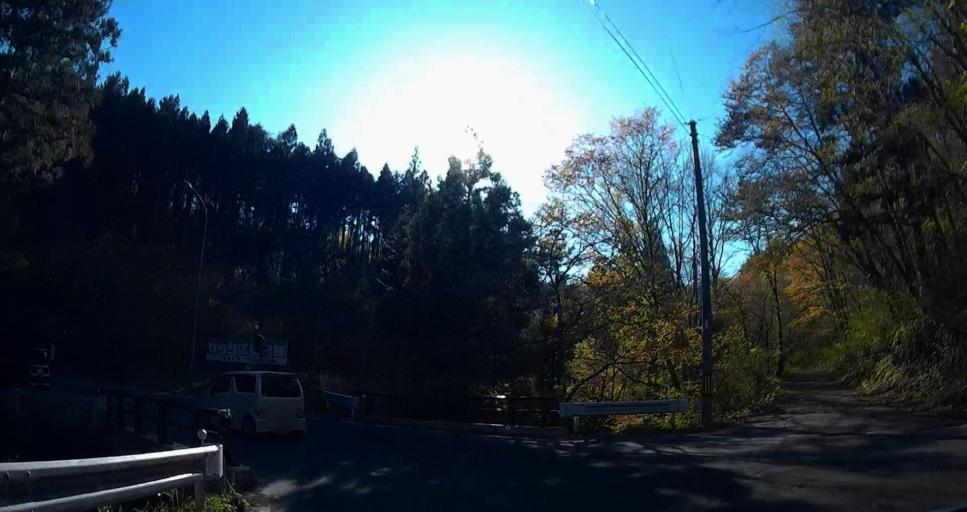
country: JP
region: Aomori
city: Mutsu
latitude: 41.4231
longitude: 141.1452
